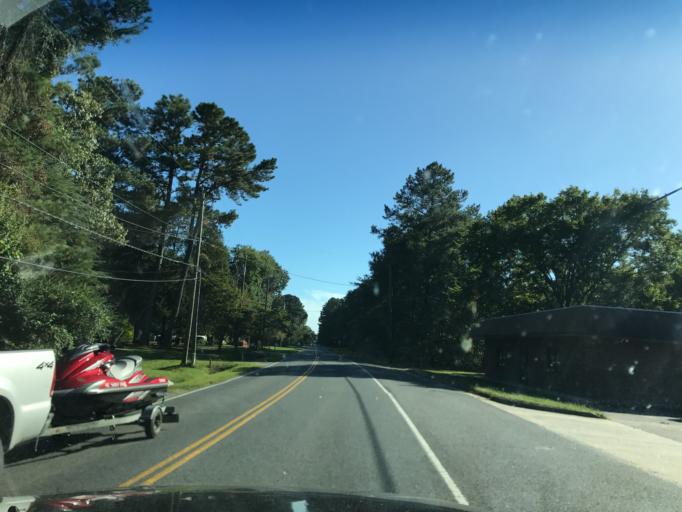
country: US
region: Virginia
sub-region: City of Portsmouth
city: Portsmouth Heights
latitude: 36.7384
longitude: -76.3451
